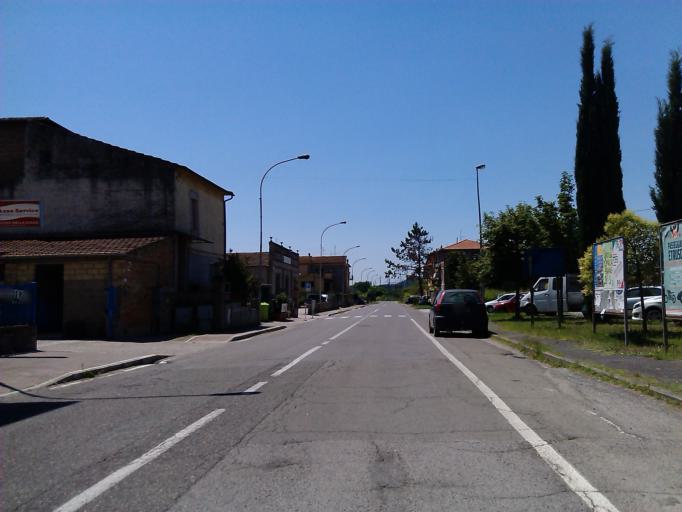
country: IT
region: Umbria
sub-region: Provincia di Terni
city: Fabro Scalo
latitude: 42.8736
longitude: 12.0422
